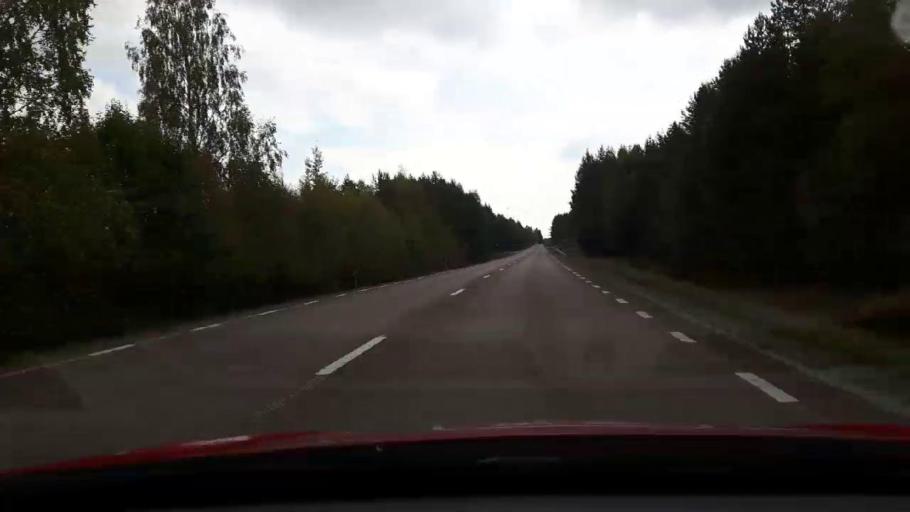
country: SE
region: Gaevleborg
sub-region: Bollnas Kommun
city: Kilafors
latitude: 61.2691
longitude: 16.5419
